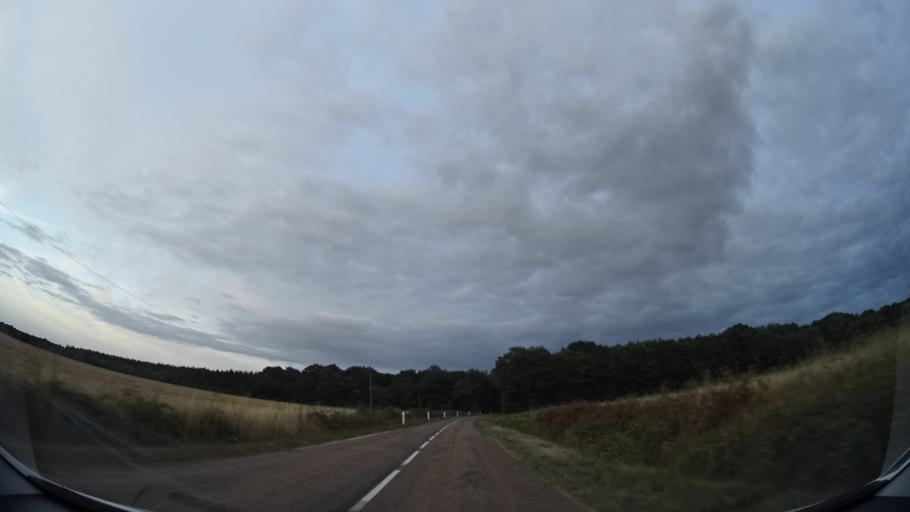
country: FR
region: Bourgogne
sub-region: Departement de l'Yonne
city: Aillant-sur-Tholon
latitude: 47.9215
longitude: 3.3022
